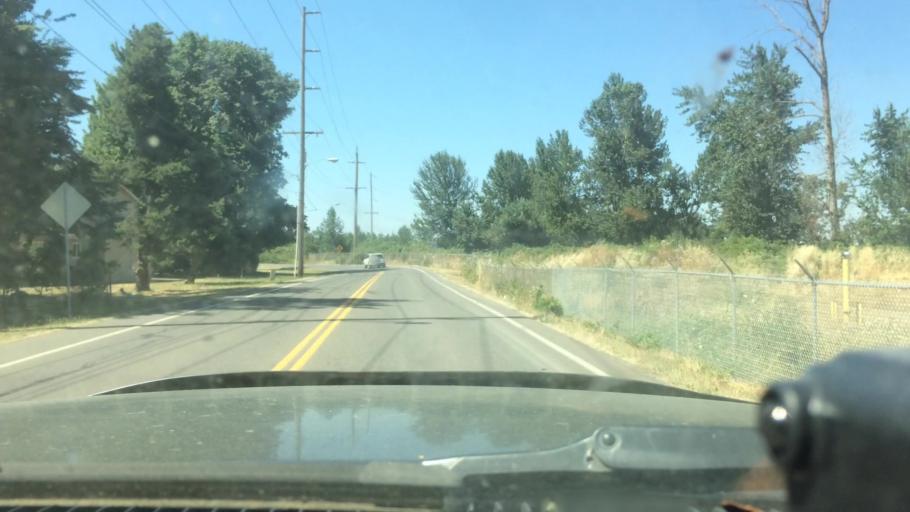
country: US
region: Oregon
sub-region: Lane County
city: Eugene
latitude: 44.1013
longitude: -123.1145
